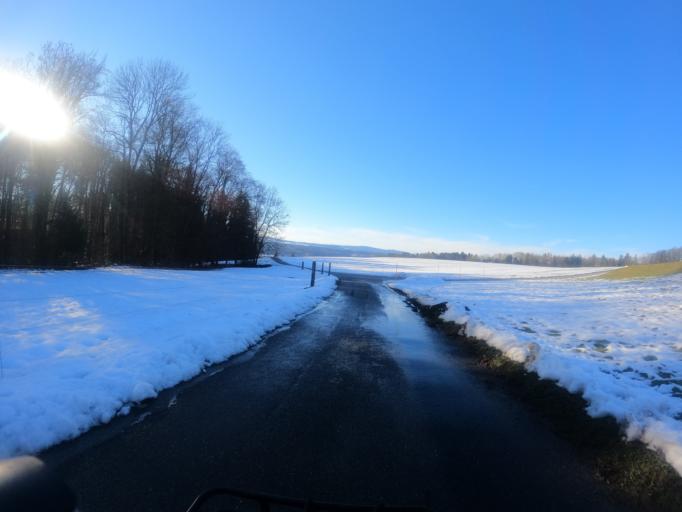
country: CH
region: Aargau
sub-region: Bezirk Bremgarten
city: Oberlunkhofen
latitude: 47.3234
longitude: 8.3929
